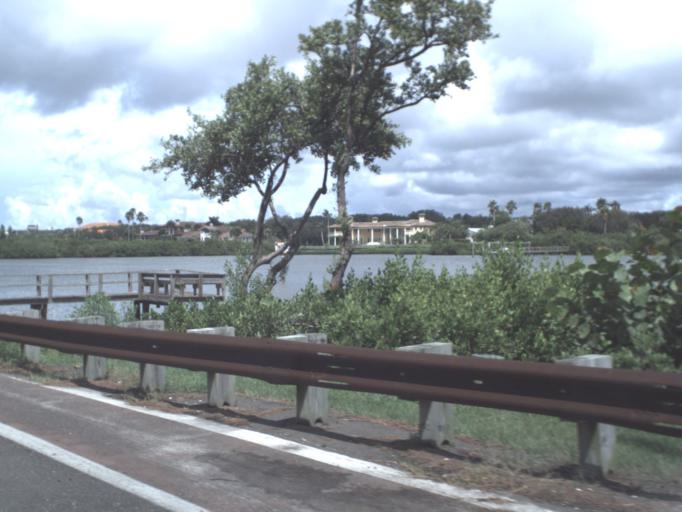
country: US
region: Florida
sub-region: Pinellas County
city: Indian Shores
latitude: 27.8685
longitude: -82.8492
